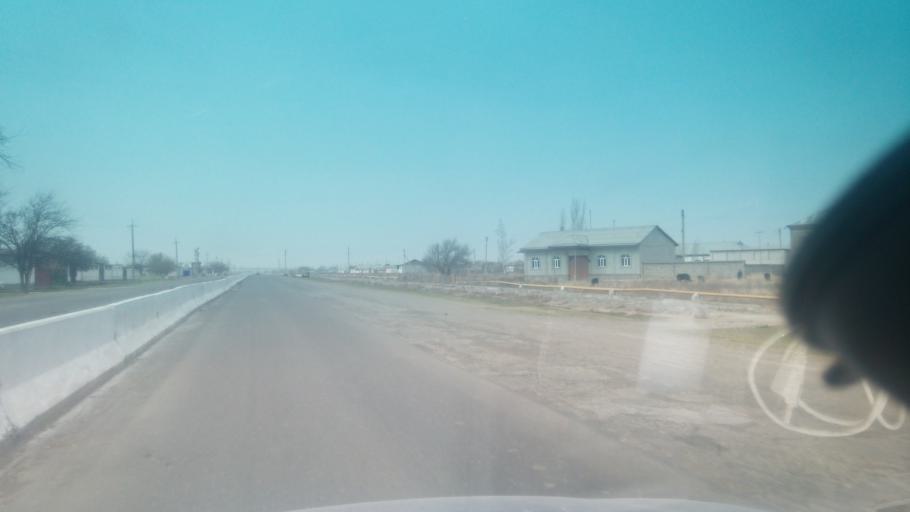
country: UZ
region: Sirdaryo
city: Yangiyer
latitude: 40.2240
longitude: 68.8279
